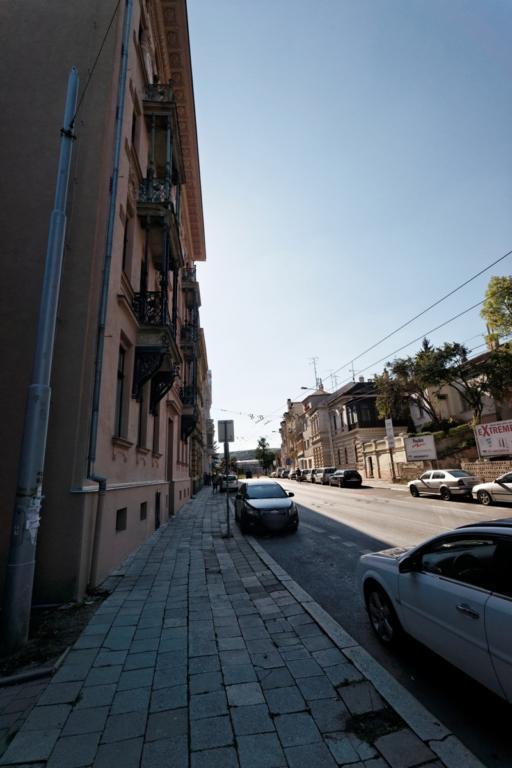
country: CZ
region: South Moravian
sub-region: Mesto Brno
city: Brno
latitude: 49.1904
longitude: 16.5906
